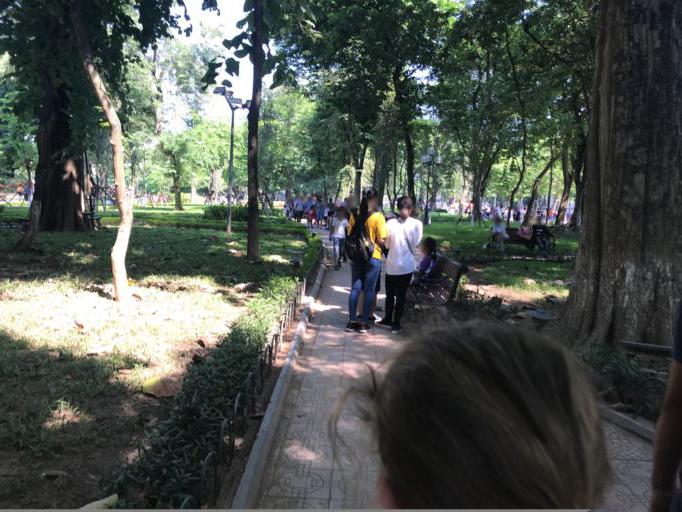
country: VN
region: Ha Noi
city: Hoan Kiem
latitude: 21.0293
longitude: 105.8536
